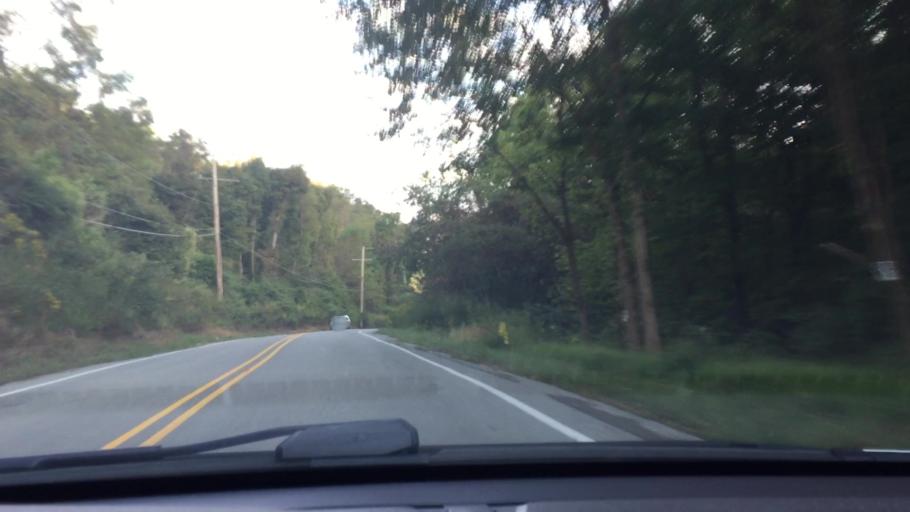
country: US
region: Pennsylvania
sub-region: Westmoreland County
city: Murrysville
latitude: 40.4491
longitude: -79.7228
